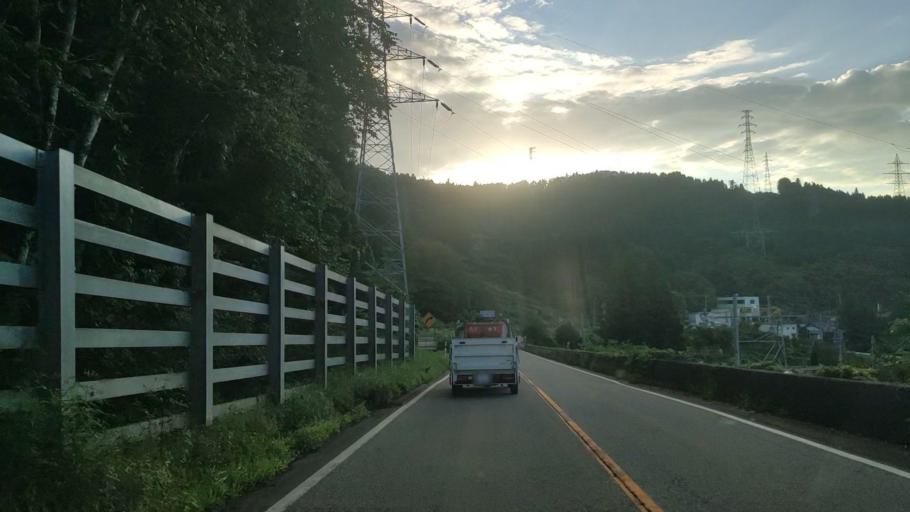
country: JP
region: Toyama
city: Nanto-shi
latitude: 36.5633
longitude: 136.9969
